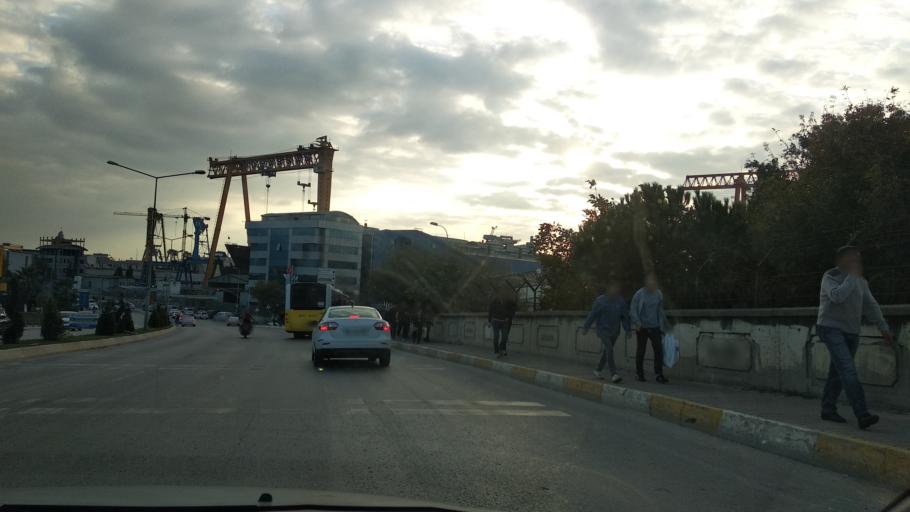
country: TR
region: Istanbul
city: Icmeler
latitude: 40.8472
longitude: 29.2945
